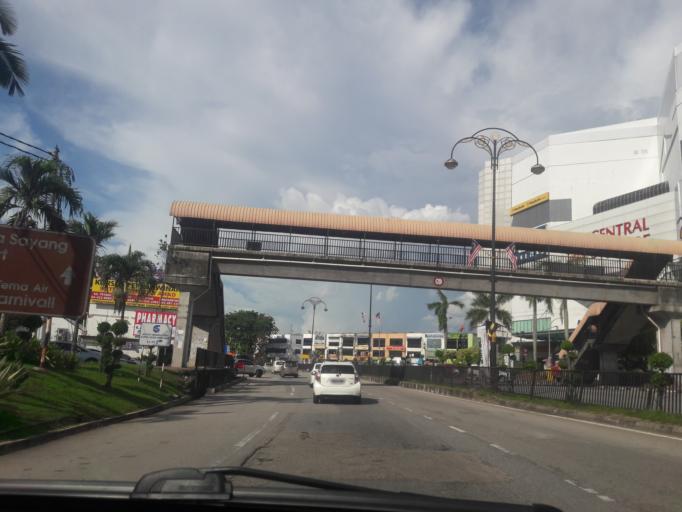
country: MY
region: Kedah
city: Sungai Petani
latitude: 5.6366
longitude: 100.4876
